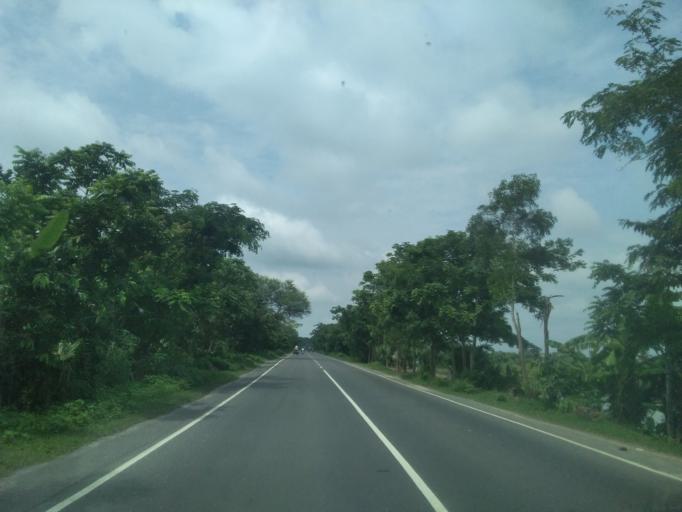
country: BD
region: Khulna
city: Kesabpur
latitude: 22.8009
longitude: 89.2312
